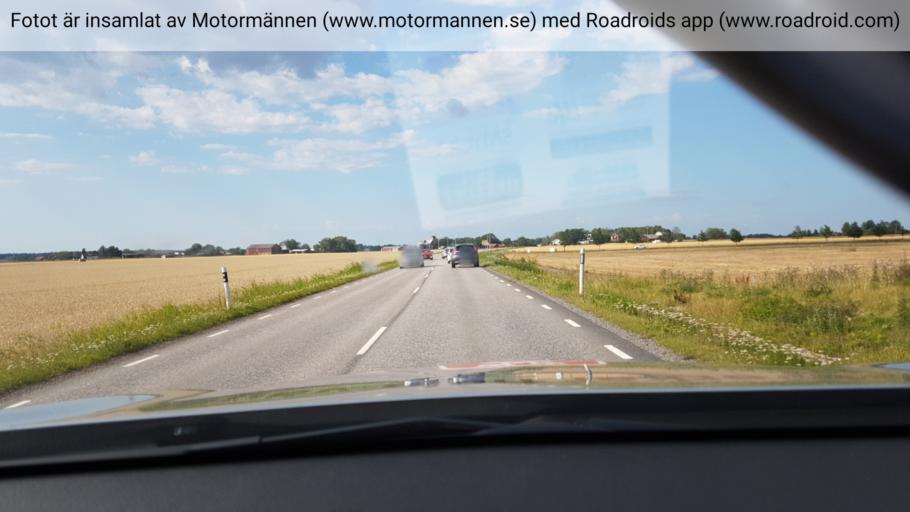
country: SE
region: Vaestra Goetaland
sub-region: Lidkopings Kommun
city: Lidkoping
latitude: 58.5406
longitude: 13.1134
